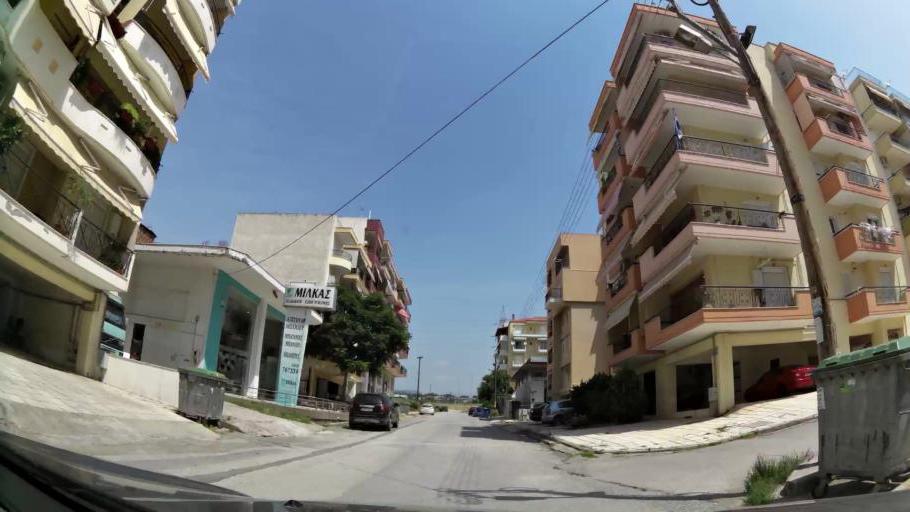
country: GR
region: Central Macedonia
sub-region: Nomos Thessalonikis
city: Evosmos
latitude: 40.6764
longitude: 22.9038
